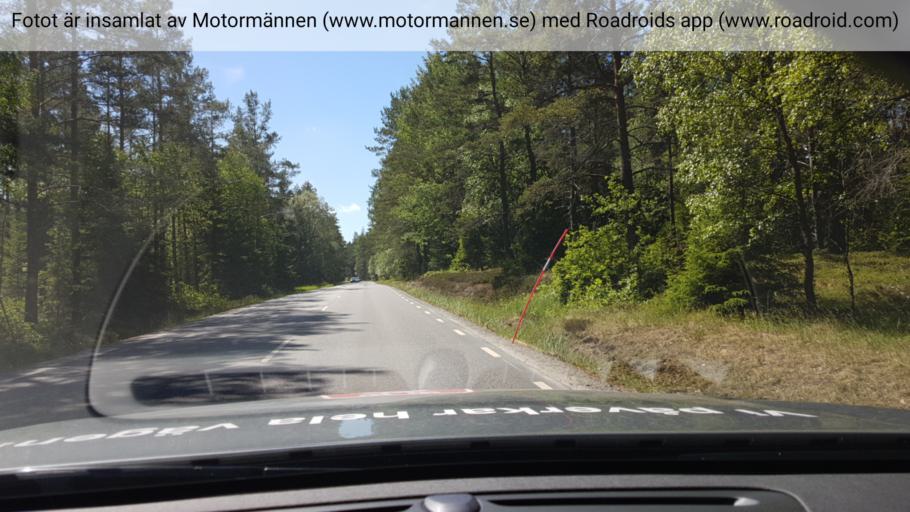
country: SE
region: Stockholm
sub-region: Haninge Kommun
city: Haninge
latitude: 59.1606
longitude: 18.1817
